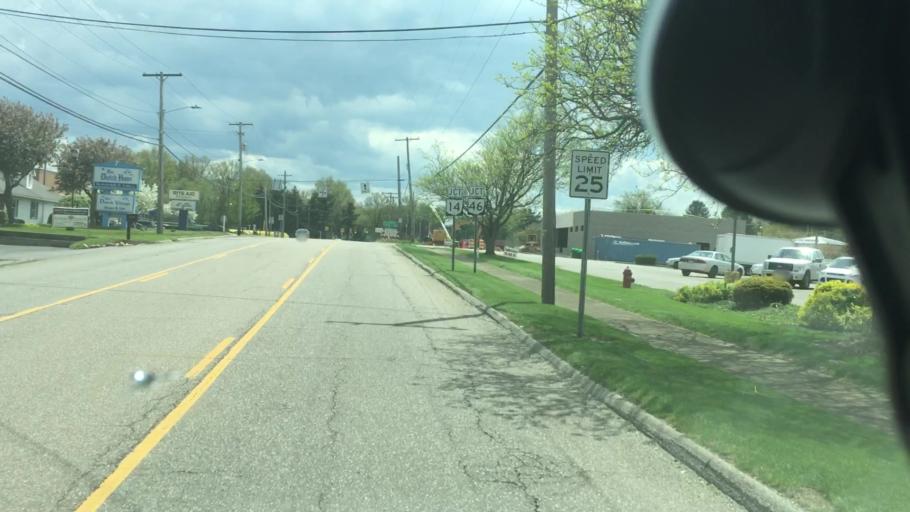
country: US
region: Ohio
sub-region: Columbiana County
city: Columbiana
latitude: 40.9021
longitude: -80.6964
